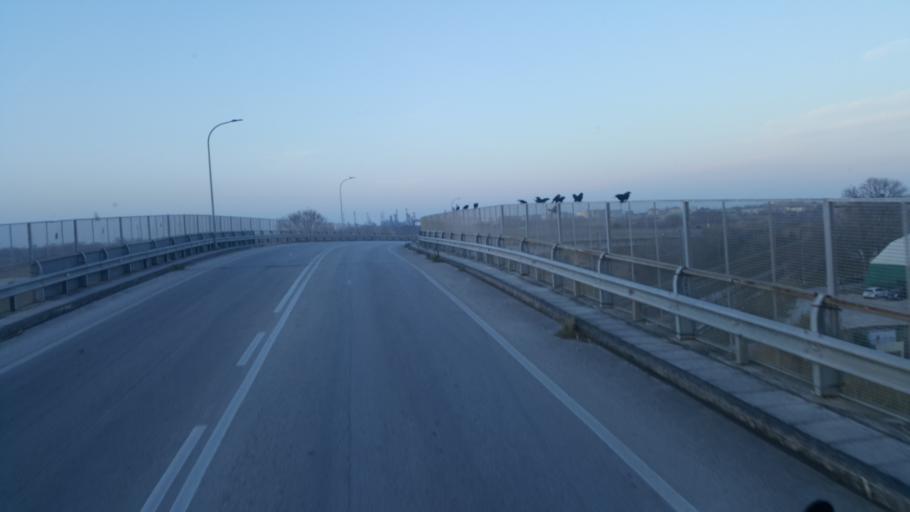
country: IT
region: The Marches
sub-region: Provincia di Ancona
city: Falconara Marittima
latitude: 43.6228
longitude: 13.3776
